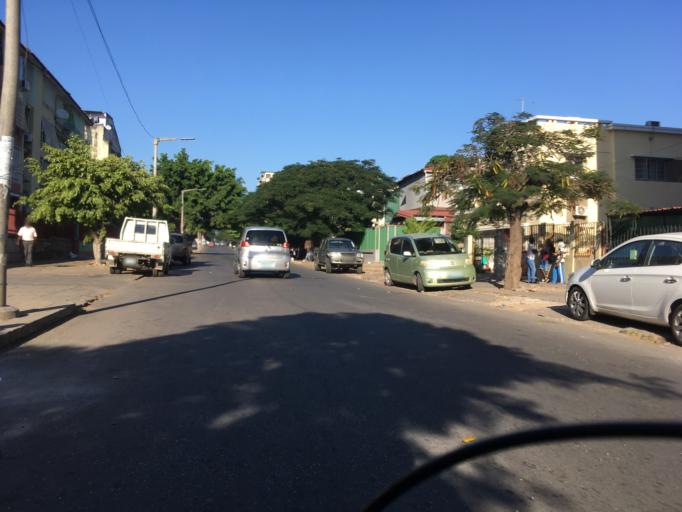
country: MZ
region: Maputo City
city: Maputo
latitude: -25.9607
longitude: 32.5802
